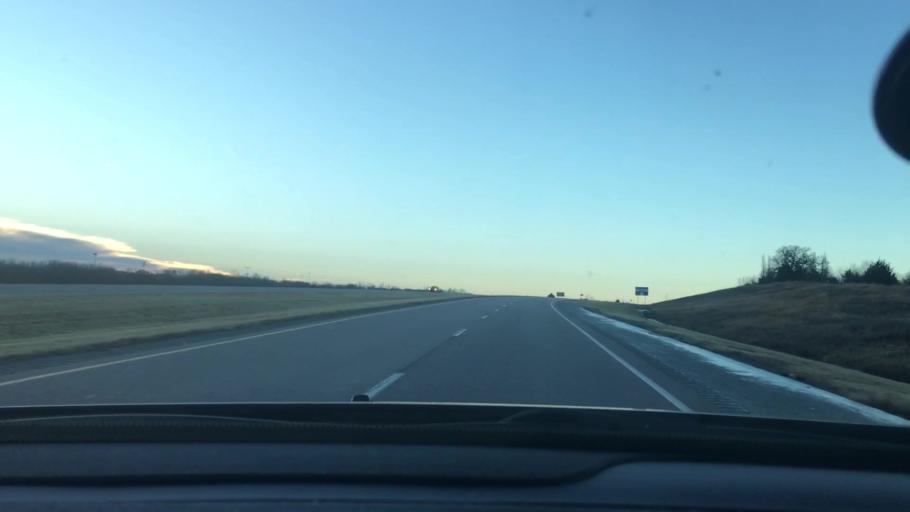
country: US
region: Oklahoma
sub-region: Pontotoc County
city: Ada
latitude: 34.8074
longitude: -96.6957
